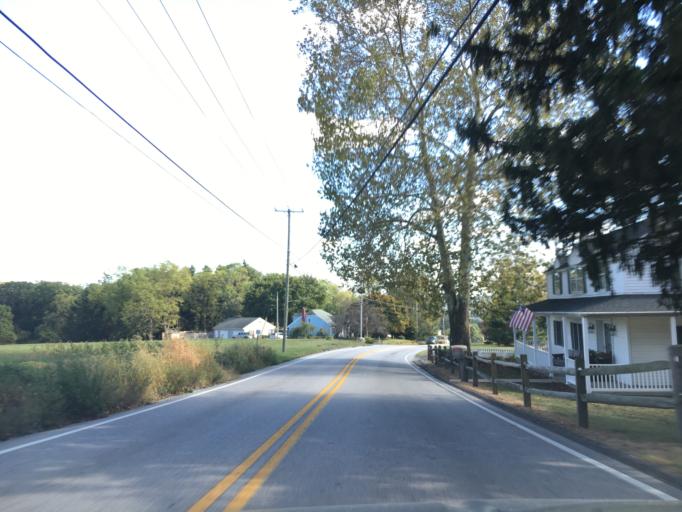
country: US
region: Pennsylvania
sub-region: York County
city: East York
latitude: 39.9989
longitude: -76.6784
